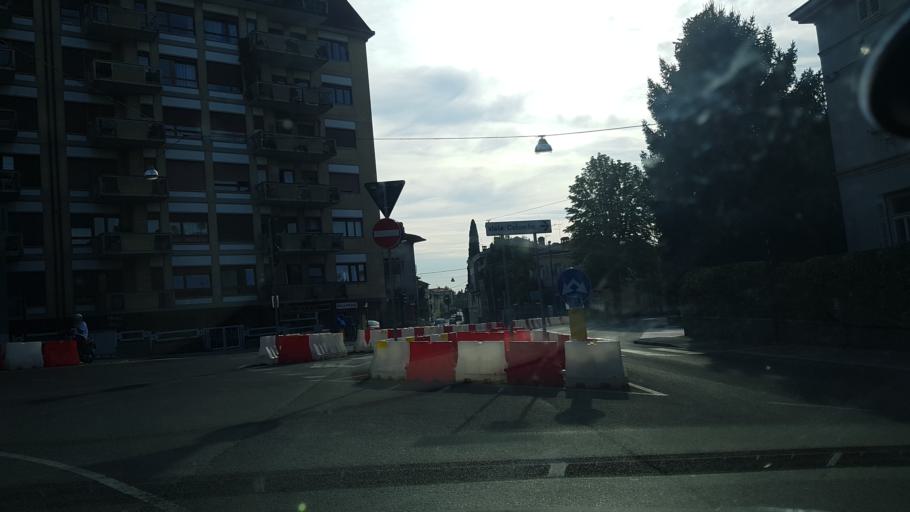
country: IT
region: Friuli Venezia Giulia
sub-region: Provincia di Gorizia
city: Gorizia
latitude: 45.9428
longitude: 13.6137
